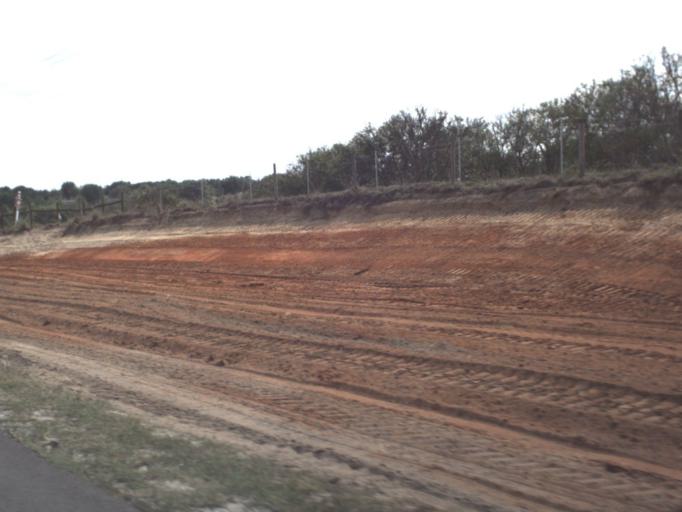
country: US
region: Florida
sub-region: Lake County
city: Four Corners
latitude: 28.4085
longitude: -81.6999
